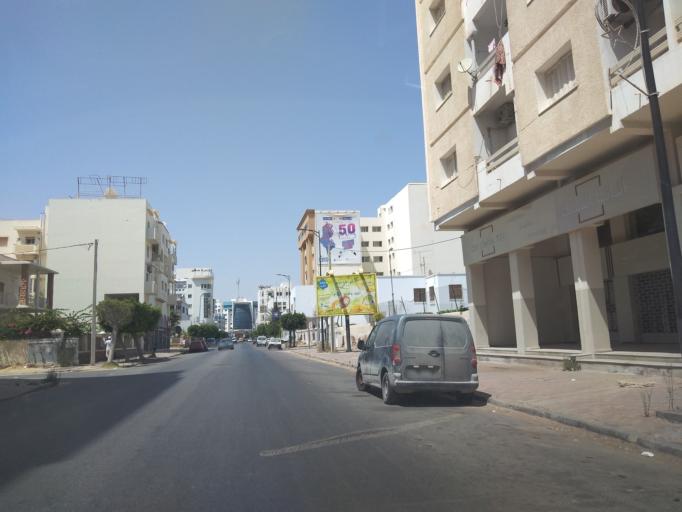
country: TN
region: Safaqis
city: Sfax
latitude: 34.7460
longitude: 10.7623
